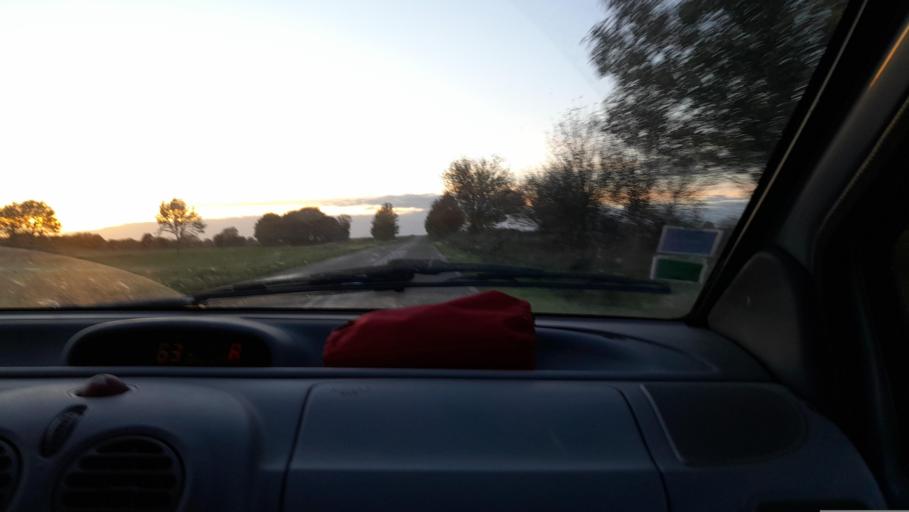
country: FR
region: Pays de la Loire
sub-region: Departement de la Mayenne
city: Ballots
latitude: 47.9018
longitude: -1.1137
